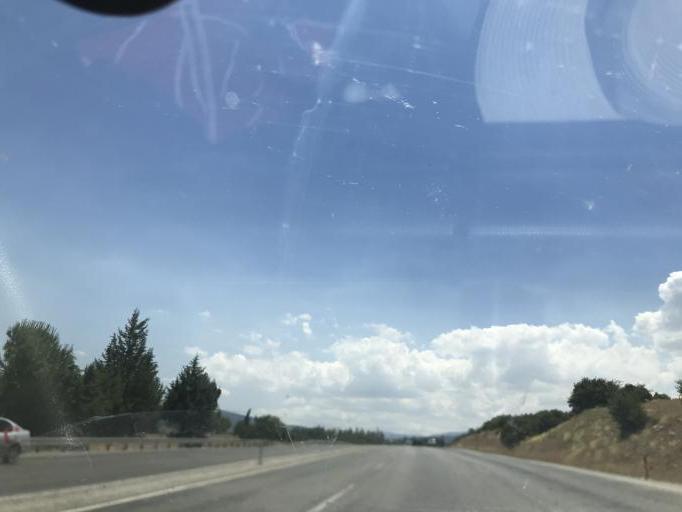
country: TR
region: Denizli
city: Honaz
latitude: 37.7095
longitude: 29.2047
